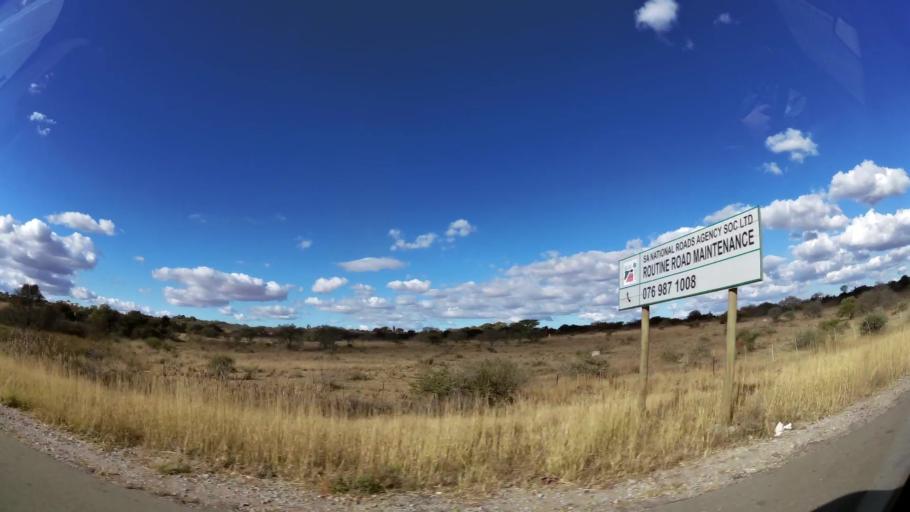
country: ZA
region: Limpopo
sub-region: Capricorn District Municipality
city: Polokwane
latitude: -23.9039
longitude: 29.5102
